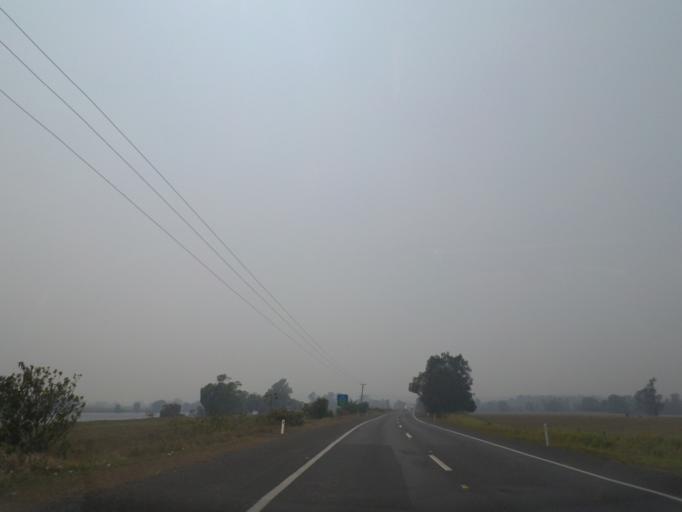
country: AU
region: New South Wales
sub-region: Clarence Valley
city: Maclean
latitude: -29.5655
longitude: 153.1232
